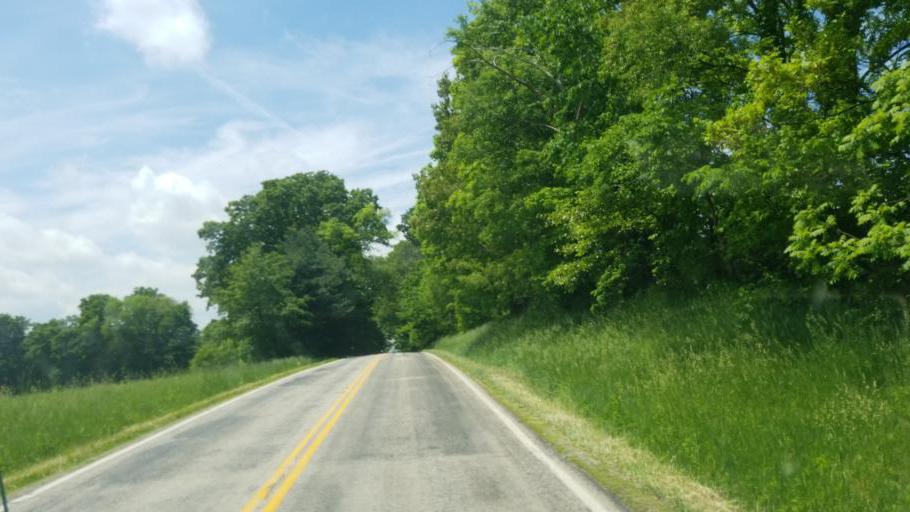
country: US
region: Ohio
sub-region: Ashland County
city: Ashland
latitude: 40.8050
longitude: -82.2178
